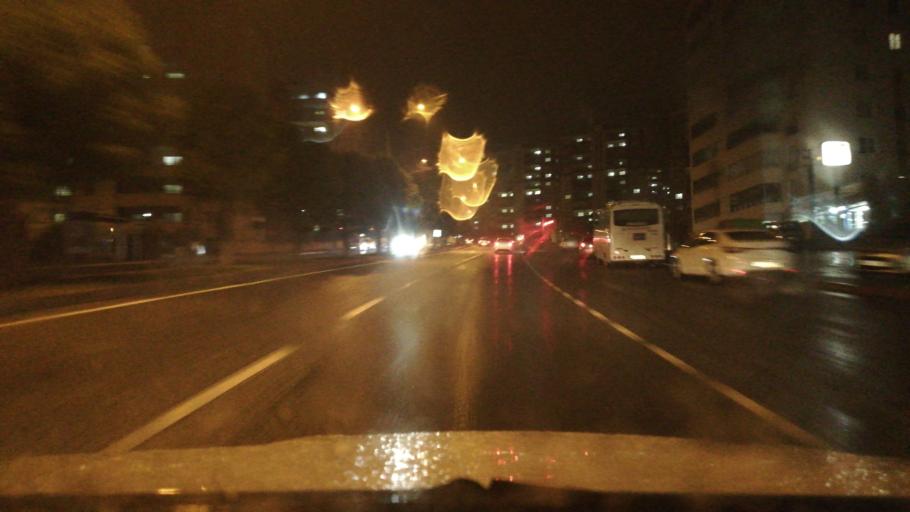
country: TR
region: Kahramanmaras
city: Kahramanmaras
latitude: 37.5963
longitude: 36.8973
